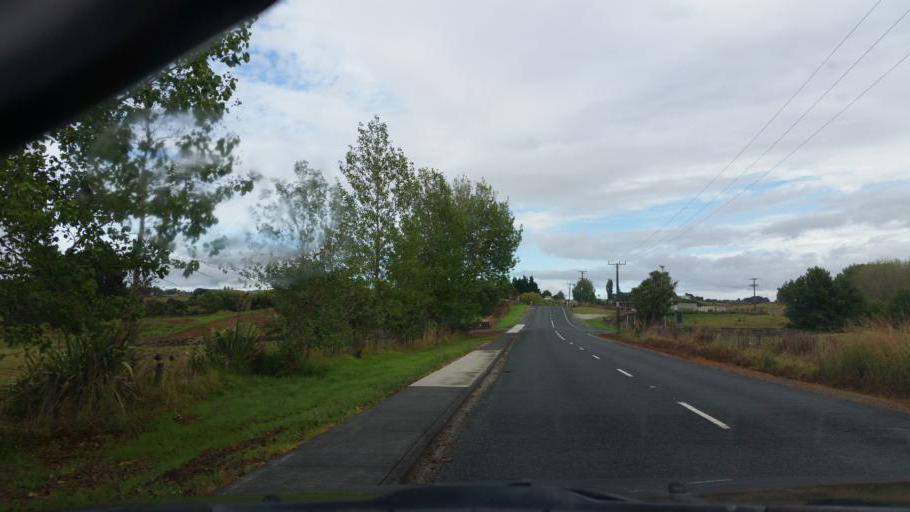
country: NZ
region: Northland
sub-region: Whangarei
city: Ruakaka
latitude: -36.1138
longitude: 174.3651
